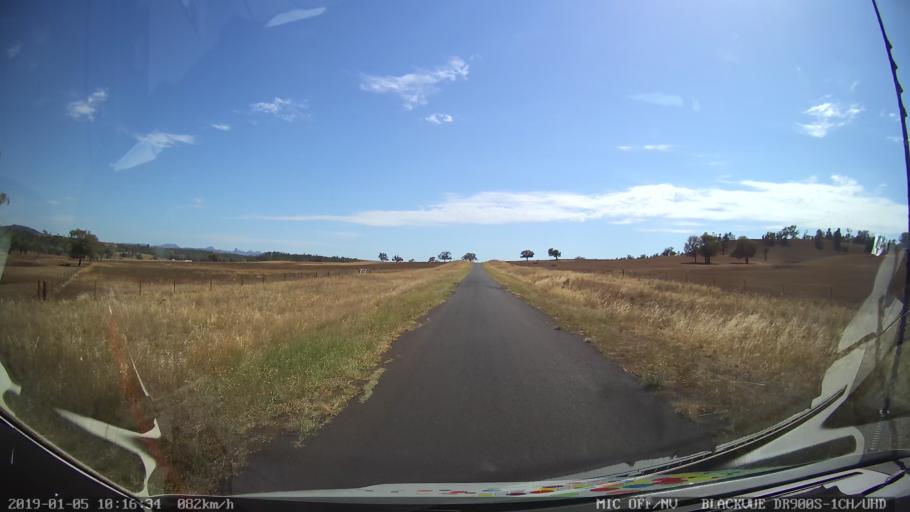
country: AU
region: New South Wales
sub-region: Gilgandra
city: Gilgandra
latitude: -31.5740
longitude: 148.9536
